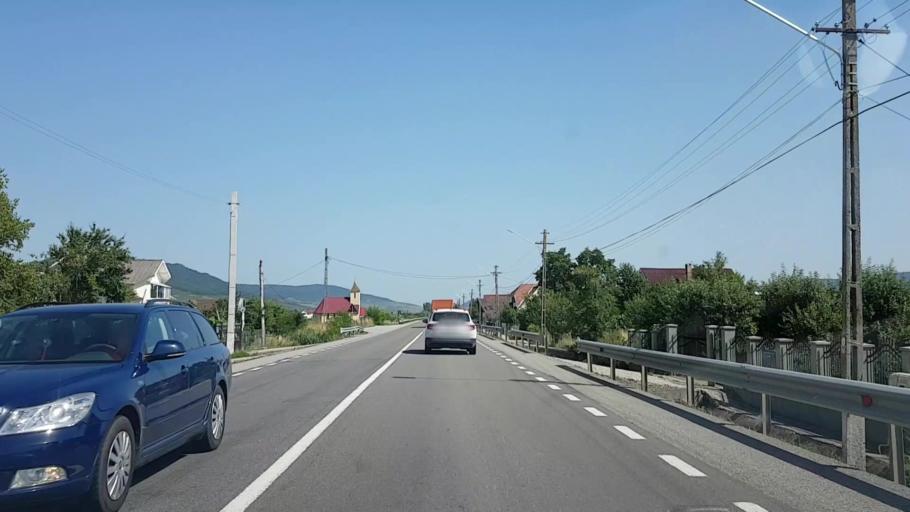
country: RO
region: Bistrita-Nasaud
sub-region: Comuna Sieu-Odorhei
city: Sieu-Odorhei
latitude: 47.1170
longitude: 24.3339
